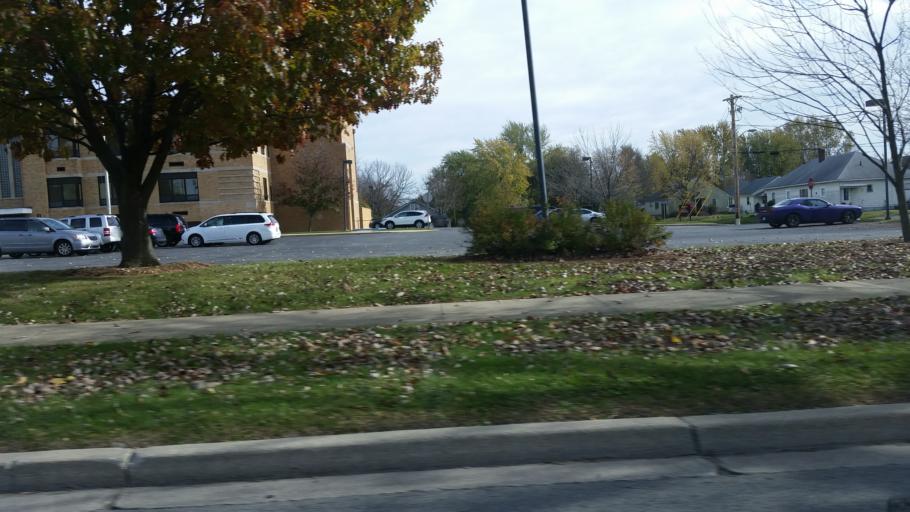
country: US
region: Indiana
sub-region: Howard County
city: Kokomo
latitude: 40.4685
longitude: -86.1338
